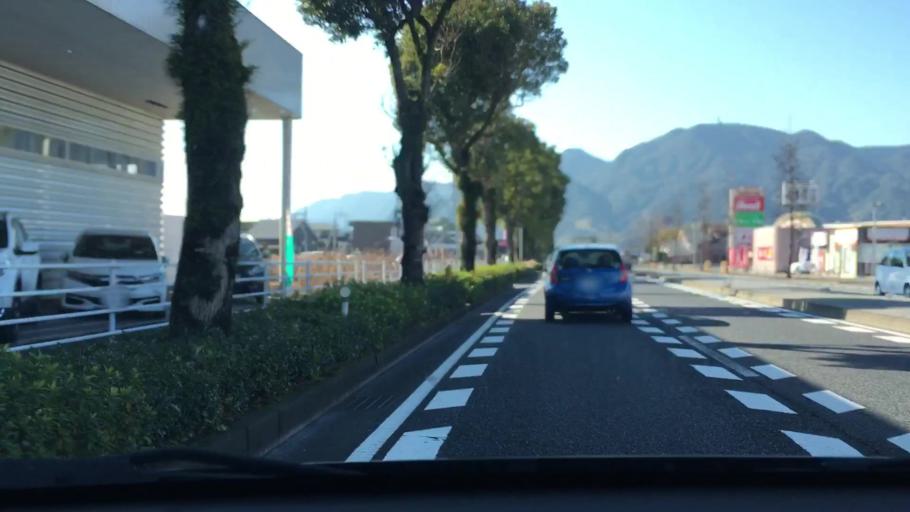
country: JP
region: Kagoshima
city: Kajiki
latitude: 31.7218
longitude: 130.6220
